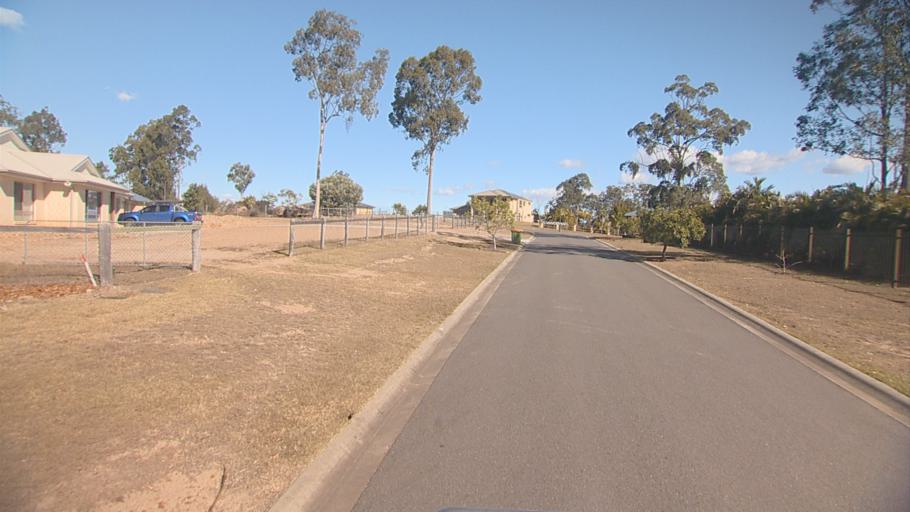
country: AU
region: Queensland
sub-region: Logan
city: North Maclean
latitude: -27.7524
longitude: 152.9344
